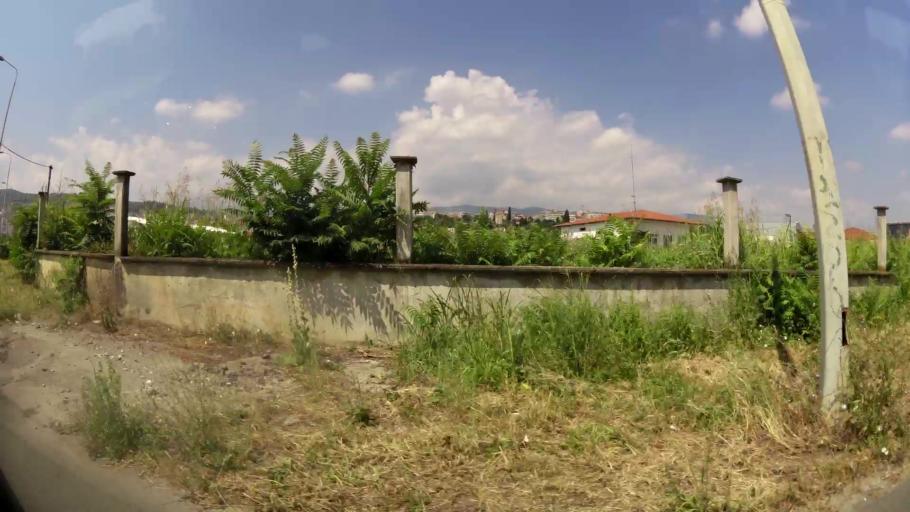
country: GR
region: Central Macedonia
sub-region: Nomos Imathias
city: Veroia
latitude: 40.5260
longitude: 22.2157
